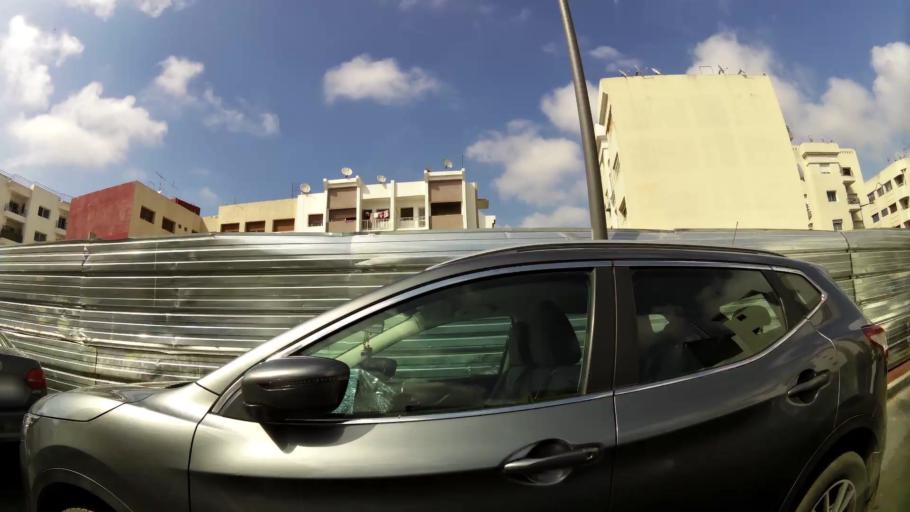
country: MA
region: Rabat-Sale-Zemmour-Zaer
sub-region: Skhirate-Temara
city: Temara
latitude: 33.9598
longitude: -6.8716
